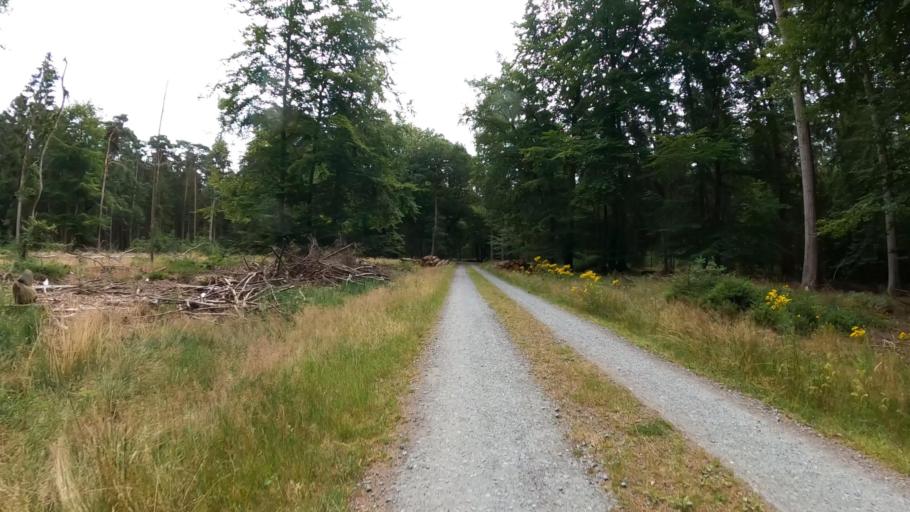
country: DE
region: Schleswig-Holstein
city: Heidmuhlen
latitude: 53.9508
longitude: 10.1164
